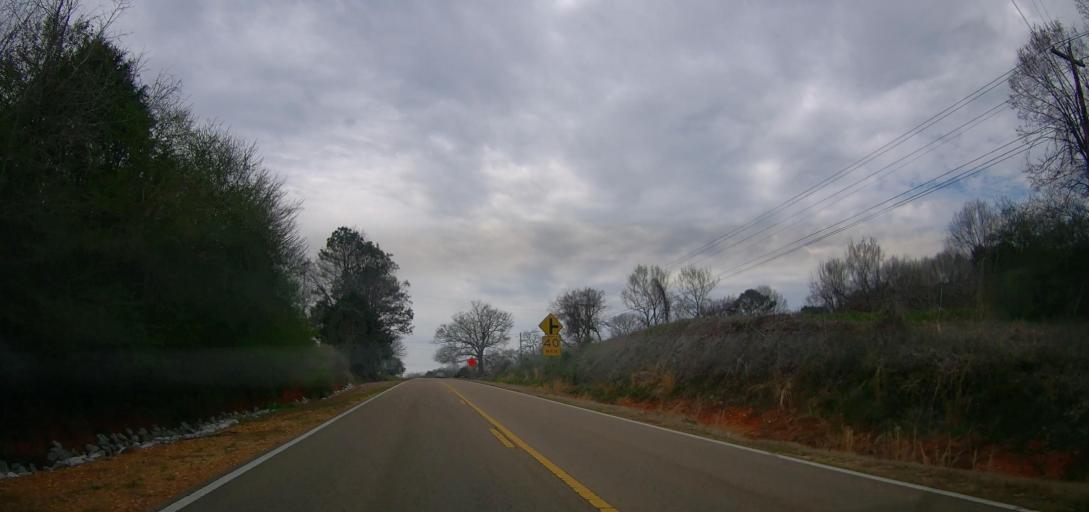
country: US
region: Mississippi
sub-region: Itawamba County
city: Fulton
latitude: 34.2779
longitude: -88.3665
